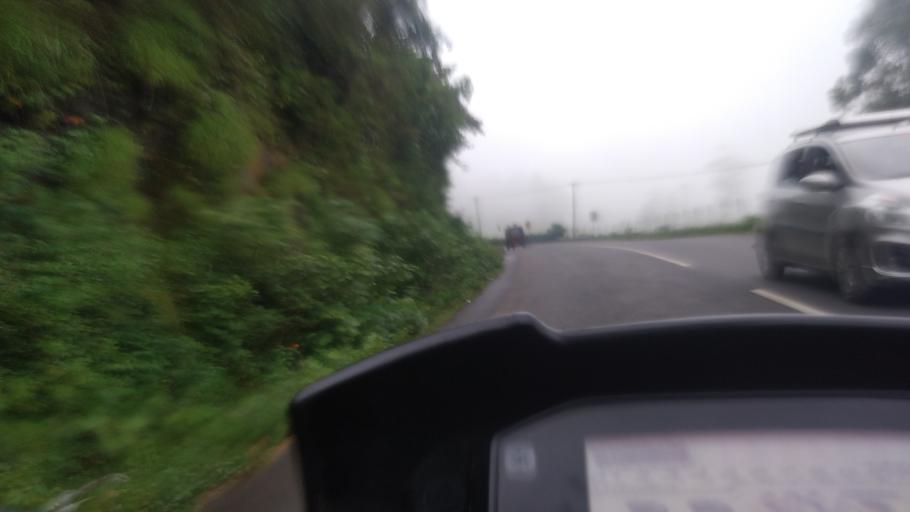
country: IN
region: Tamil Nadu
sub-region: Theni
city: Gudalur
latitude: 9.5798
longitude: 77.0390
